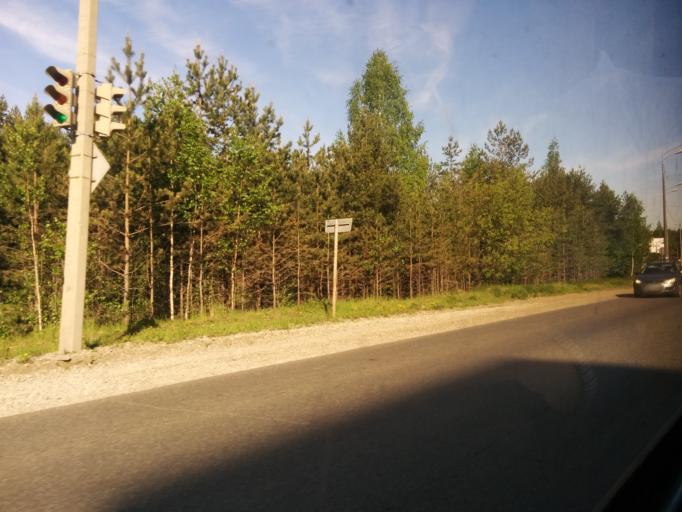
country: RU
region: Perm
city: Kondratovo
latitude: 58.0372
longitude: 56.1396
